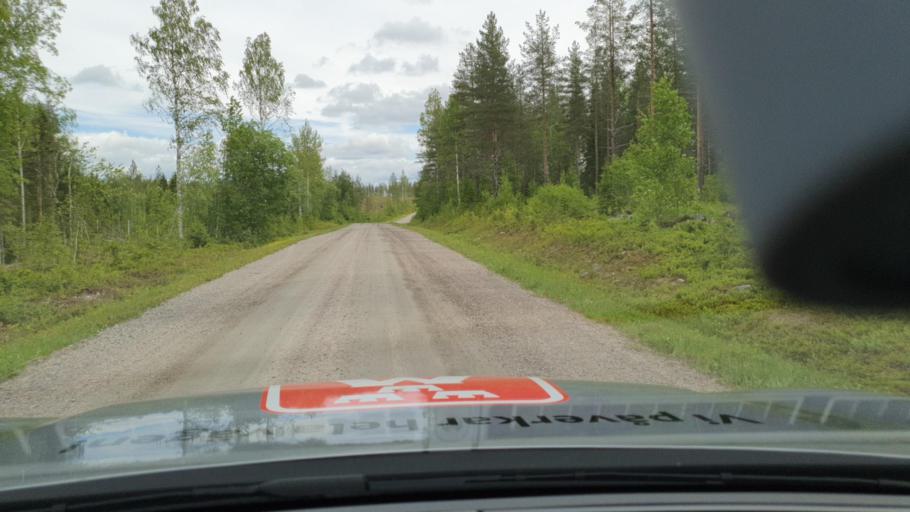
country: FI
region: Lapland
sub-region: Torniolaakso
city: Ylitornio
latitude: 65.9562
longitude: 23.6086
